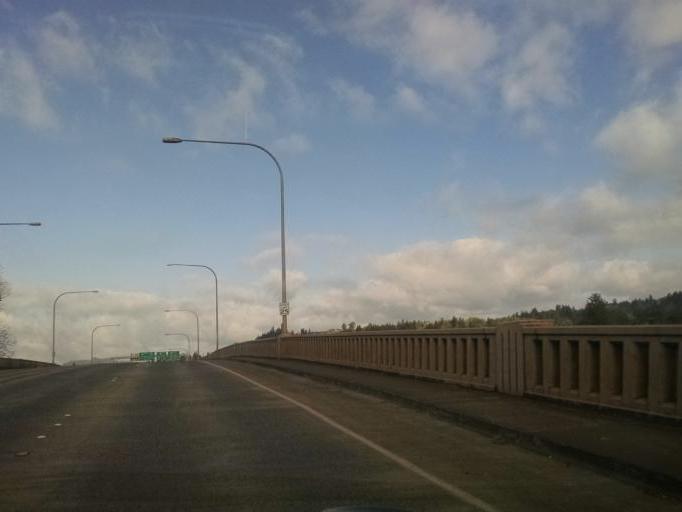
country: US
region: Washington
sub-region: Cowlitz County
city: Kelso
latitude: 46.1448
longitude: -122.9115
